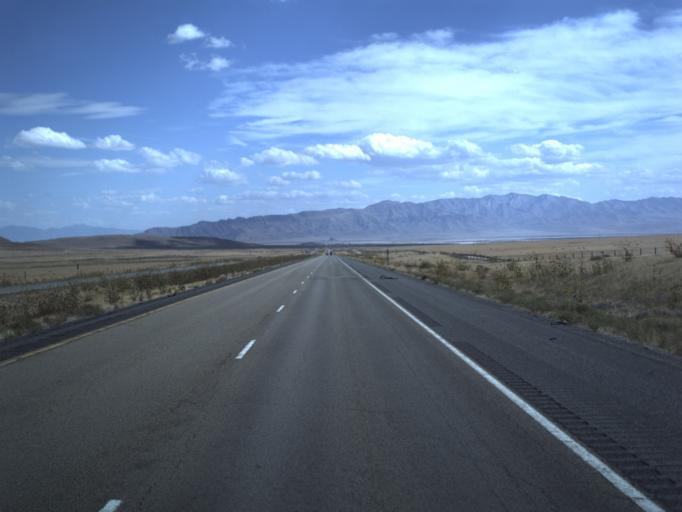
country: US
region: Utah
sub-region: Tooele County
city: Grantsville
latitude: 40.8103
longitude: -112.8686
